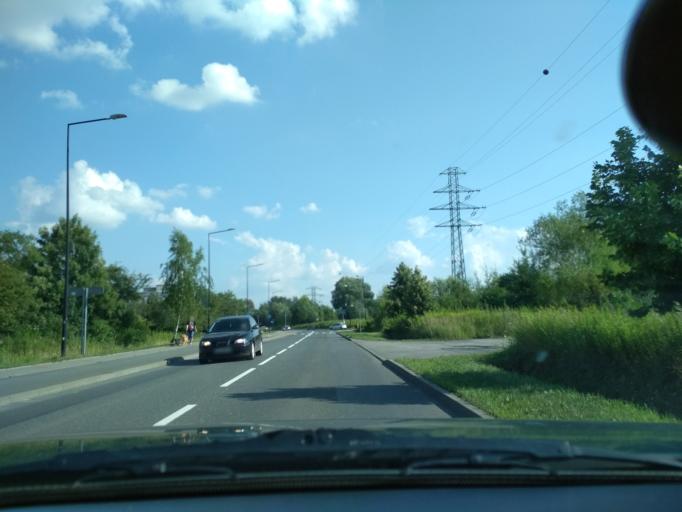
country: PL
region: Silesian Voivodeship
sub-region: Gliwice
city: Gliwice
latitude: 50.2757
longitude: 18.6822
